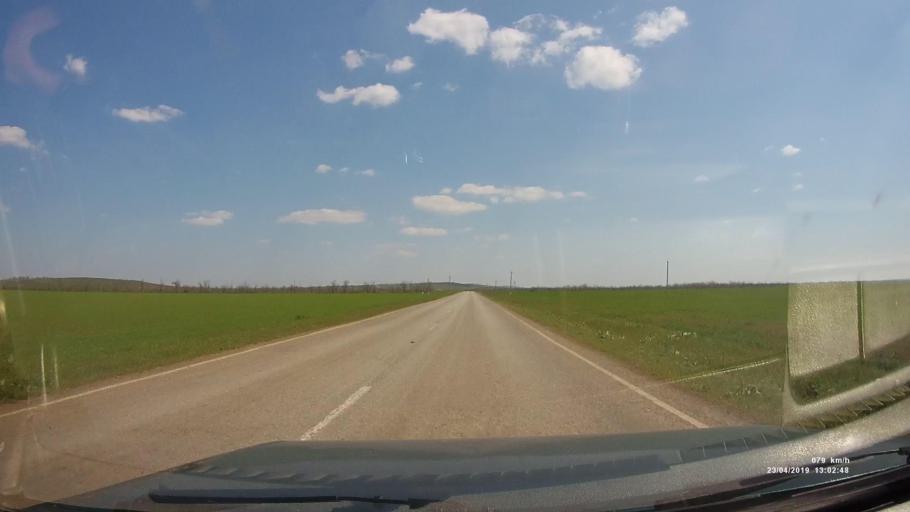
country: RU
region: Kalmykiya
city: Yashalta
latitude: 46.5991
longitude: 42.6744
